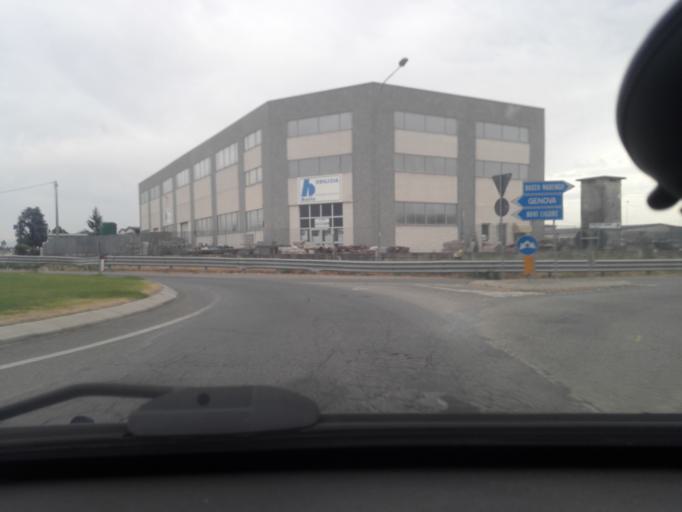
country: IT
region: Piedmont
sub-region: Provincia di Alessandria
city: Mandrogne
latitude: 44.8381
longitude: 8.7331
